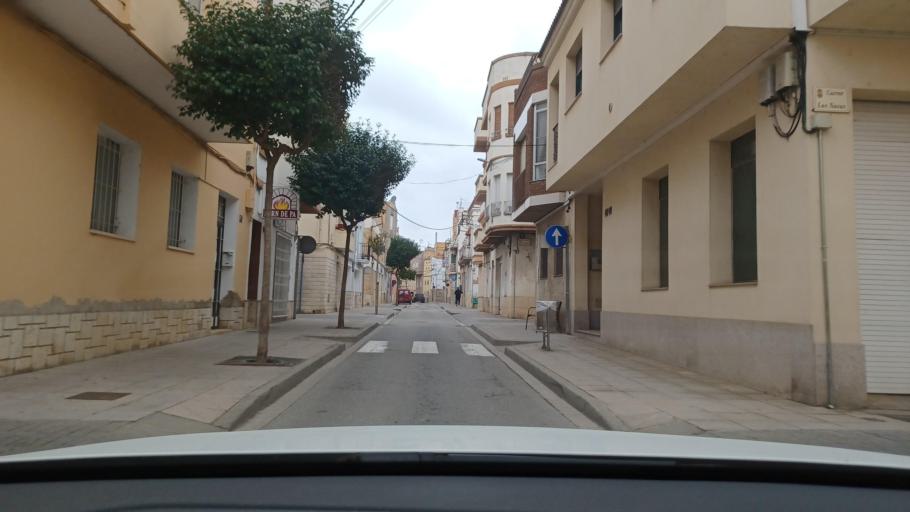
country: ES
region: Catalonia
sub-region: Provincia de Tarragona
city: Amposta
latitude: 40.7145
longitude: 0.5771
